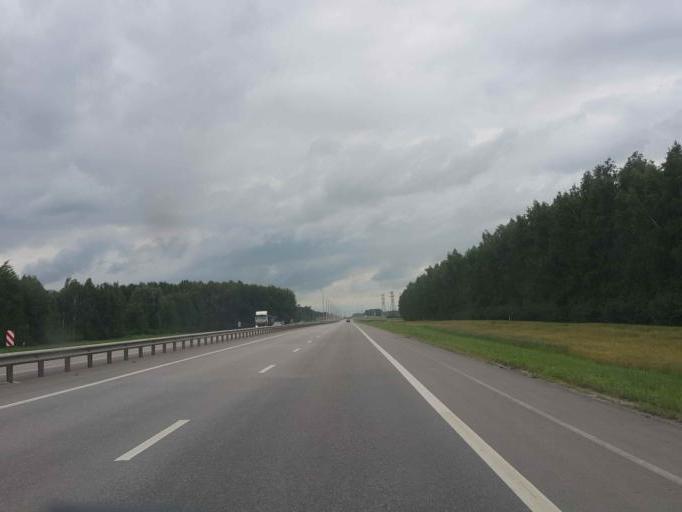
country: RU
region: Tambov
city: Zavoronezhskoye
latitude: 52.8497
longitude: 40.8029
